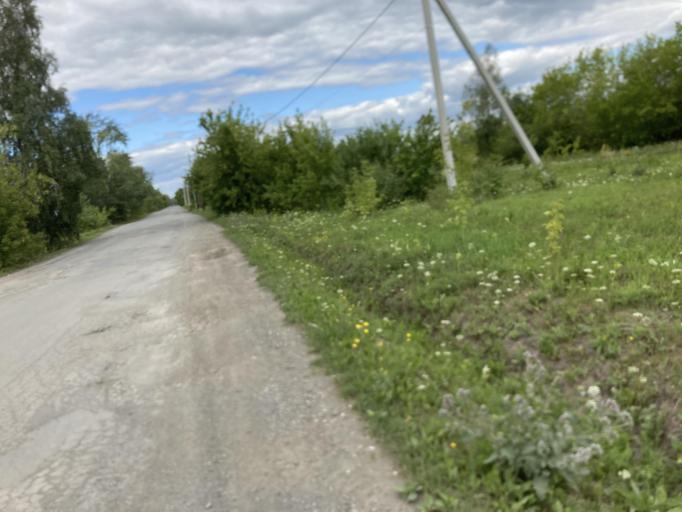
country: RU
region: Sverdlovsk
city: Bogdanovich
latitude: 56.7871
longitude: 62.0661
